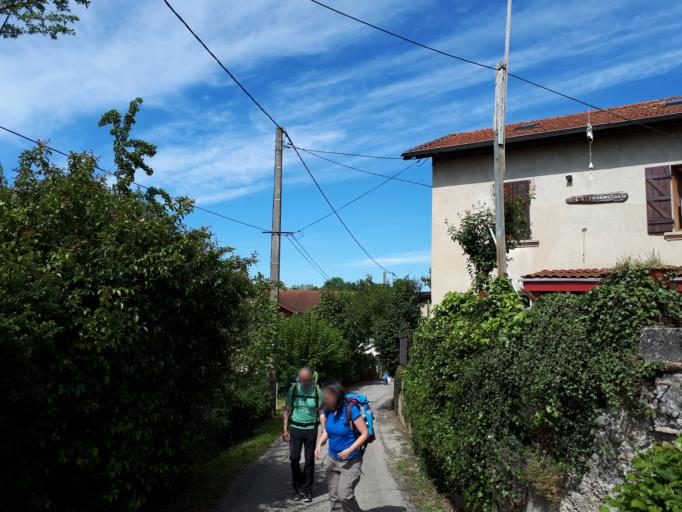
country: FR
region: Rhone-Alpes
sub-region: Departement de l'Isere
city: Saint-Savin
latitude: 45.6140
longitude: 5.2944
